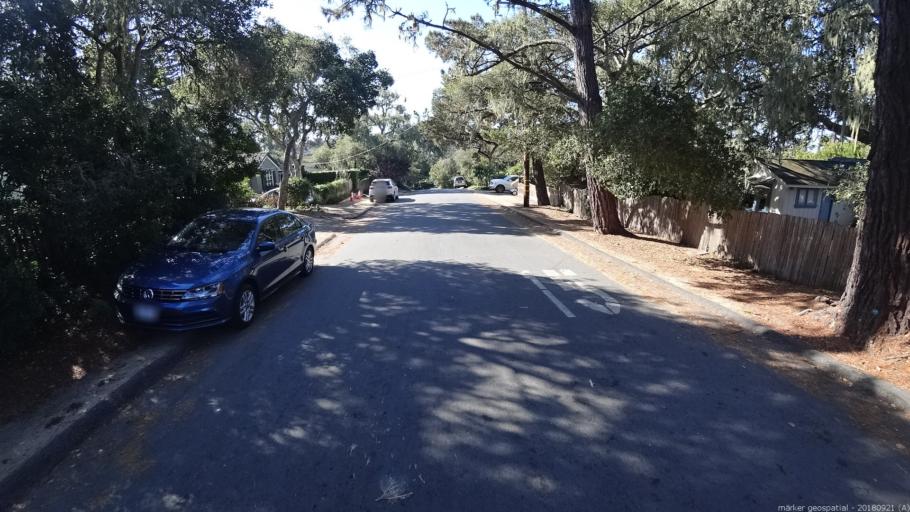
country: US
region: California
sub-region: Monterey County
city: Carmel-by-the-Sea
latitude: 36.5604
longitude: -121.9227
